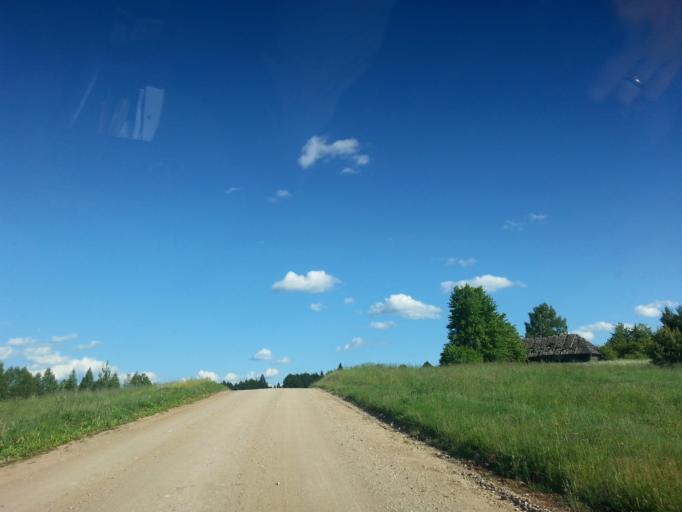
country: BY
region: Minsk
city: Narach
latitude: 54.9770
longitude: 26.6216
